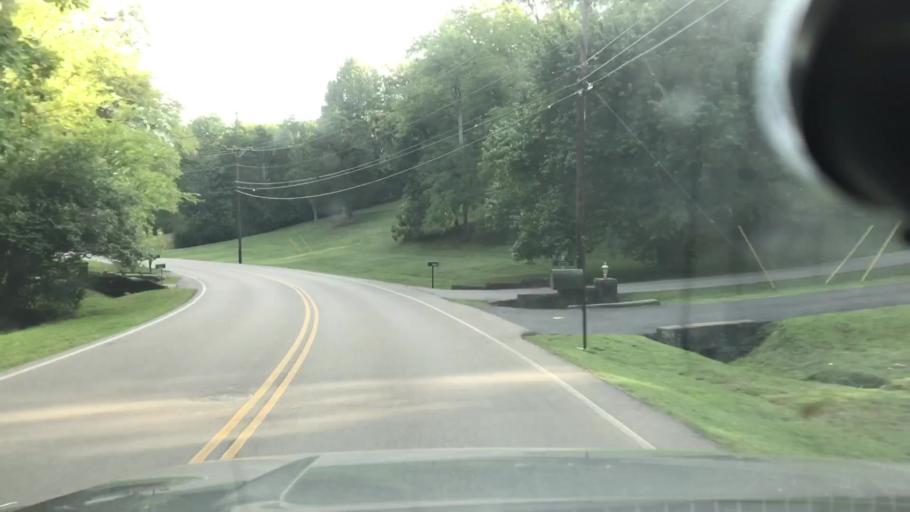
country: US
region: Tennessee
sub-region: Davidson County
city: Forest Hills
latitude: 36.0460
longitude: -86.8418
